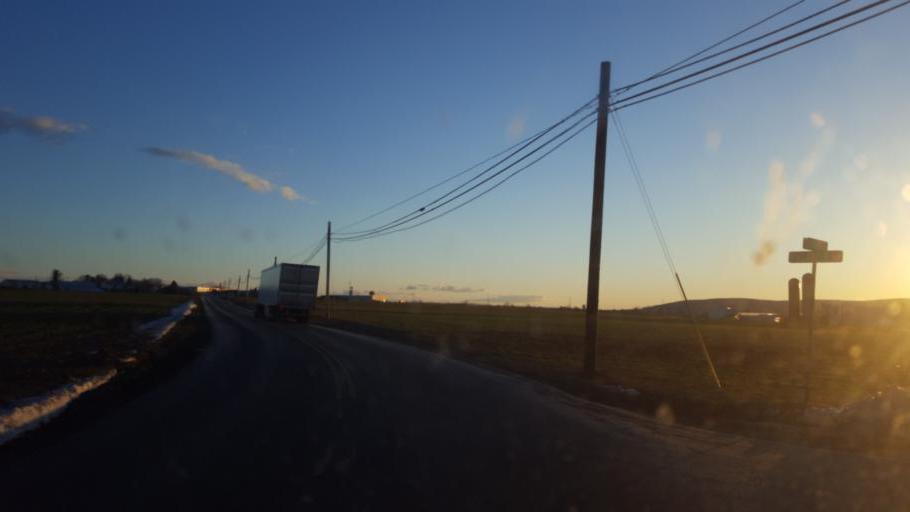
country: US
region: Pennsylvania
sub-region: Lancaster County
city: New Holland
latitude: 40.0785
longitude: -76.1031
